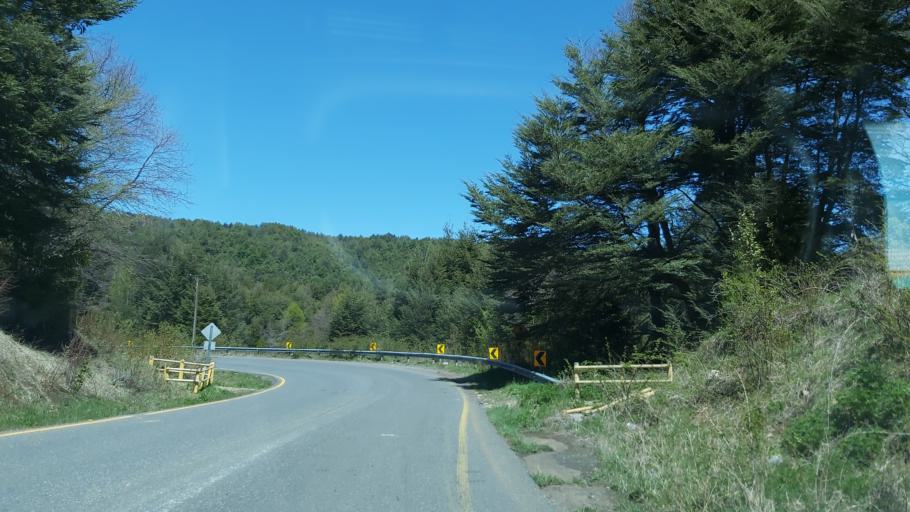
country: CL
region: Araucania
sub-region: Provincia de Cautin
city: Vilcun
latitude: -38.4687
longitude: -71.6491
